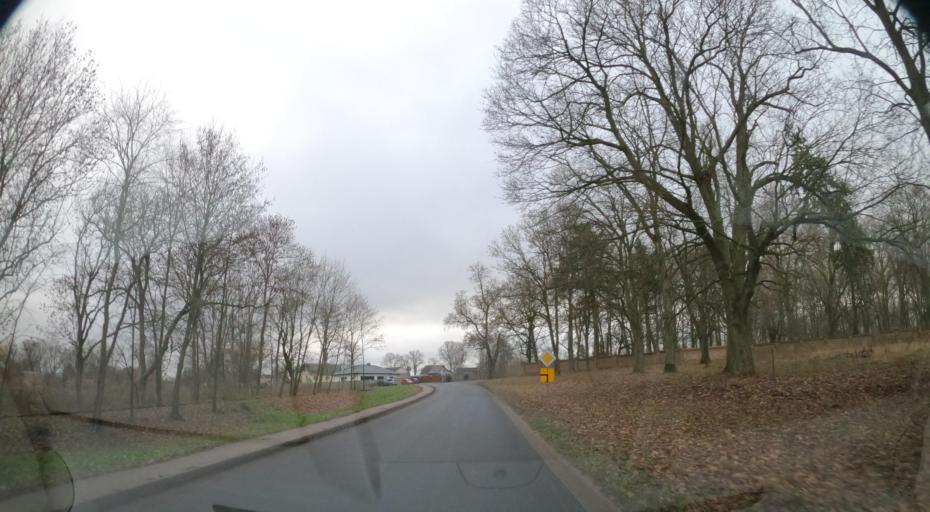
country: PL
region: Greater Poland Voivodeship
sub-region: Powiat pilski
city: Lobzenica
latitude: 53.2305
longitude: 17.3141
